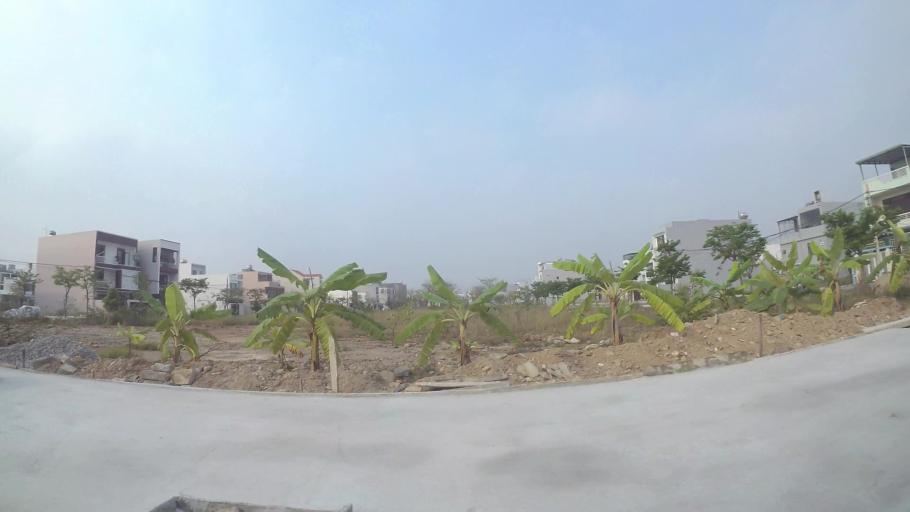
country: VN
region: Da Nang
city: Cam Le
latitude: 16.0159
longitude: 108.2204
